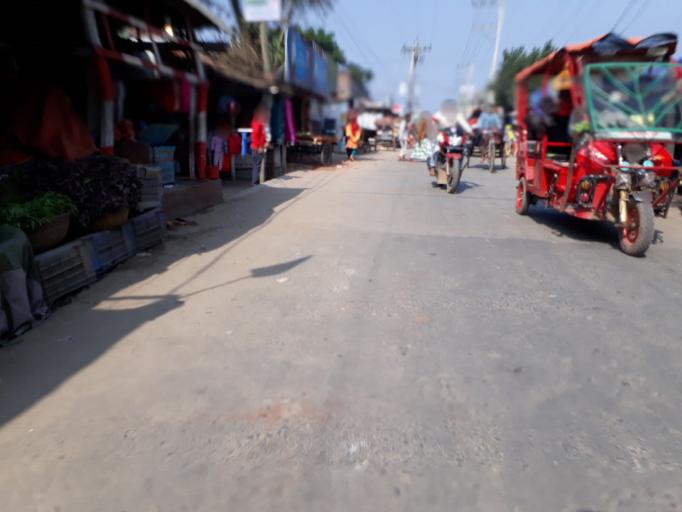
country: BD
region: Dhaka
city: Tungi
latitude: 23.8794
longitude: 90.3100
